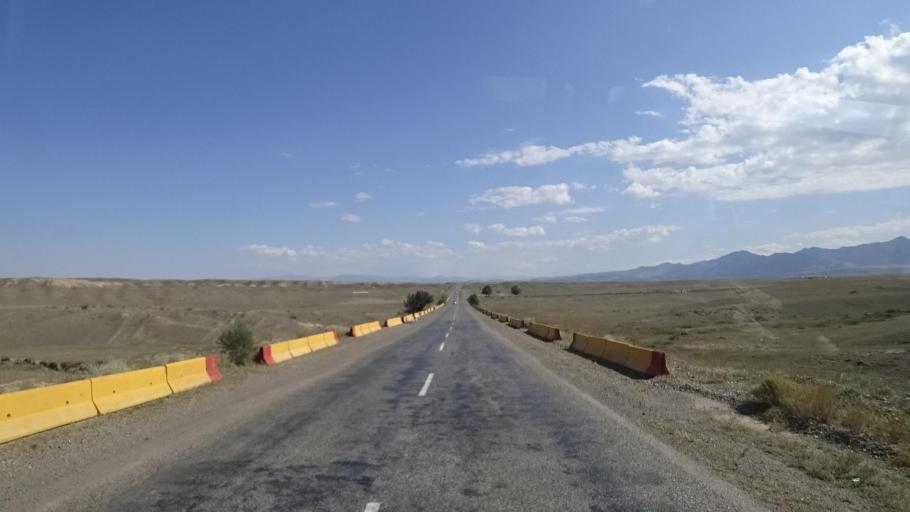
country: KZ
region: Almaty Oblysy
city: Kegen
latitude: 43.2381
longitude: 78.9950
